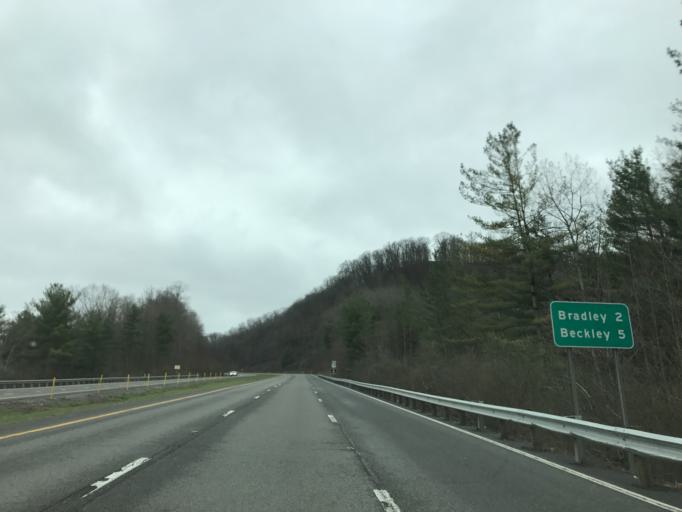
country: US
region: West Virginia
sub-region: Fayette County
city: Mount Hope
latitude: 37.8908
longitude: -81.1869
